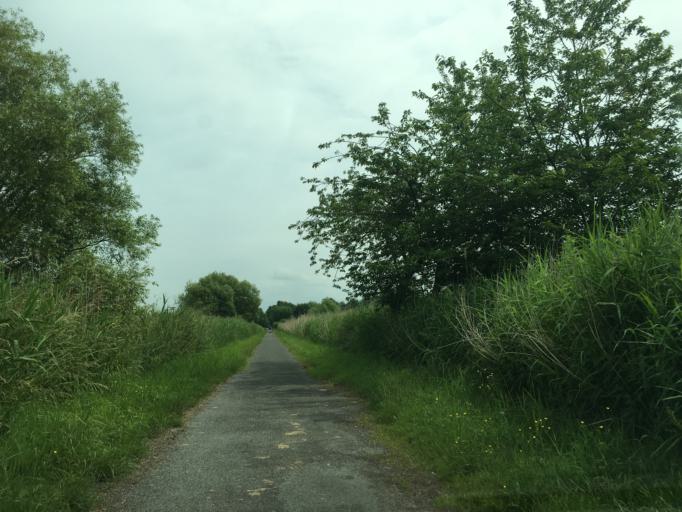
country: DE
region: North Rhine-Westphalia
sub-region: Regierungsbezirk Munster
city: Muenster
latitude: 52.0286
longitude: 7.6494
